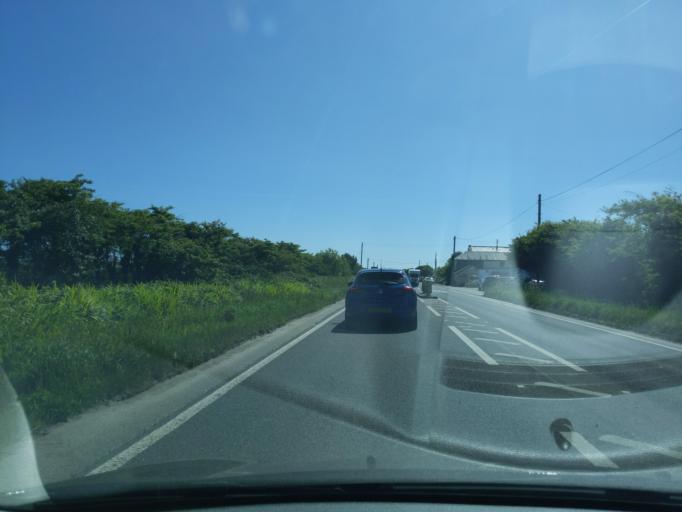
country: GB
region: England
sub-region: Cornwall
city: Wendron
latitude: 50.1559
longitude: -5.1903
